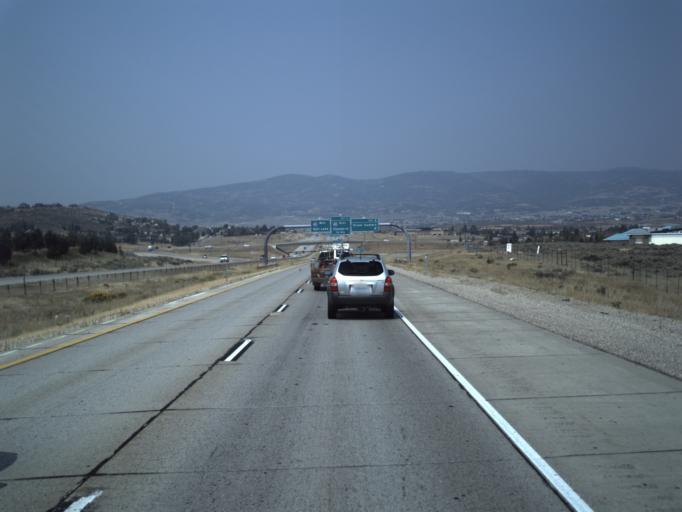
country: US
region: Utah
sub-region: Summit County
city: Snyderville
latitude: 40.7122
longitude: -111.4825
